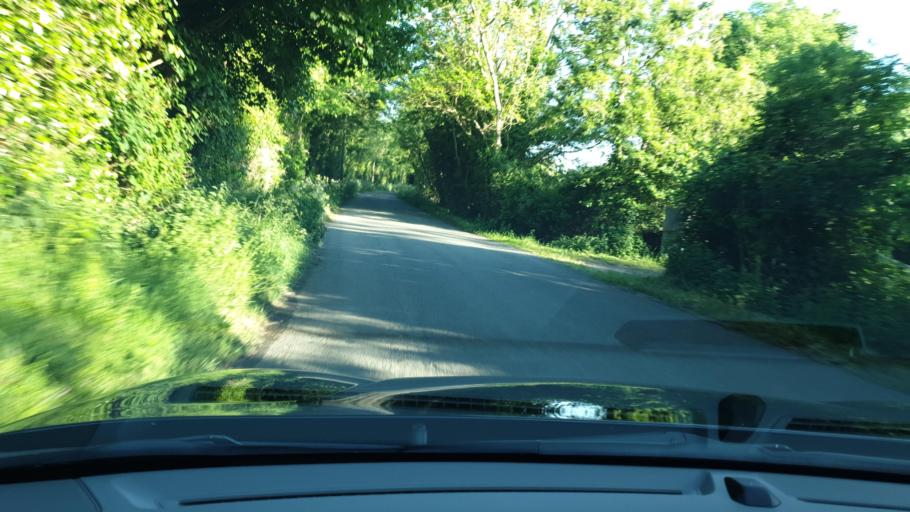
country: IE
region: Leinster
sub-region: Fingal County
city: Swords
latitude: 53.4966
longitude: -6.2313
